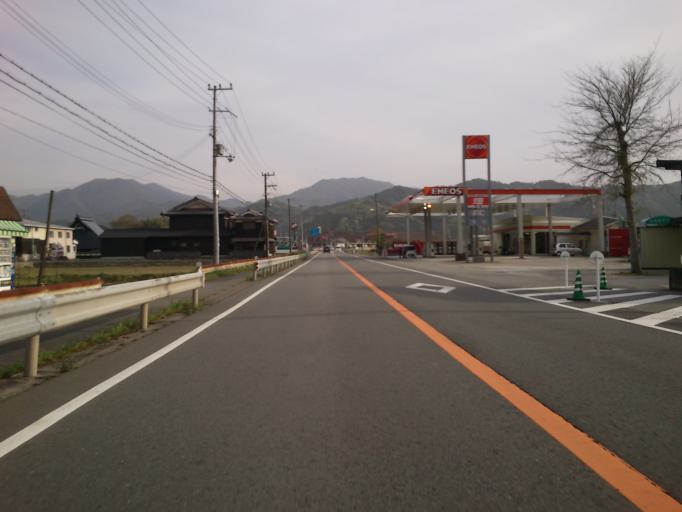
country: JP
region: Hyogo
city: Sasayama
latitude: 35.0939
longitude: 135.3152
